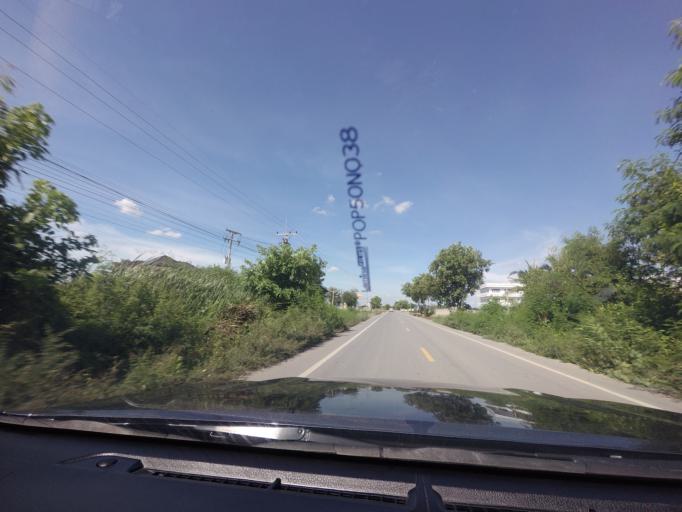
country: TH
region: Suphan Buri
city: Song Phi Nong
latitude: 14.1602
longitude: 99.9976
